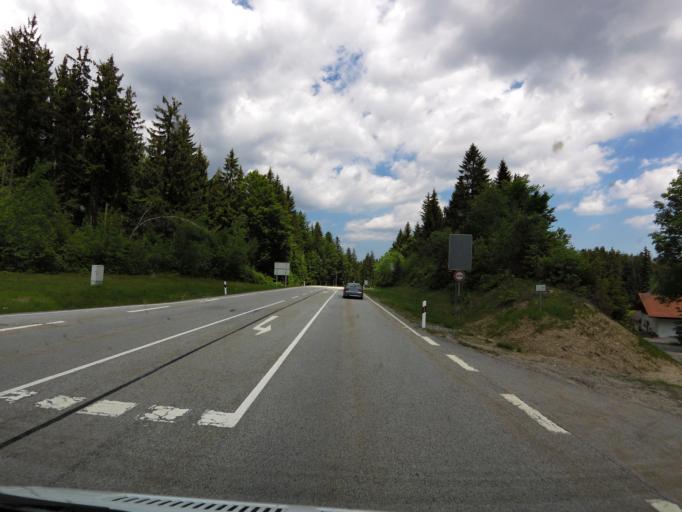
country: DE
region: Bavaria
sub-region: Lower Bavaria
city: Philippsreut
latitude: 48.8706
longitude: 13.6854
